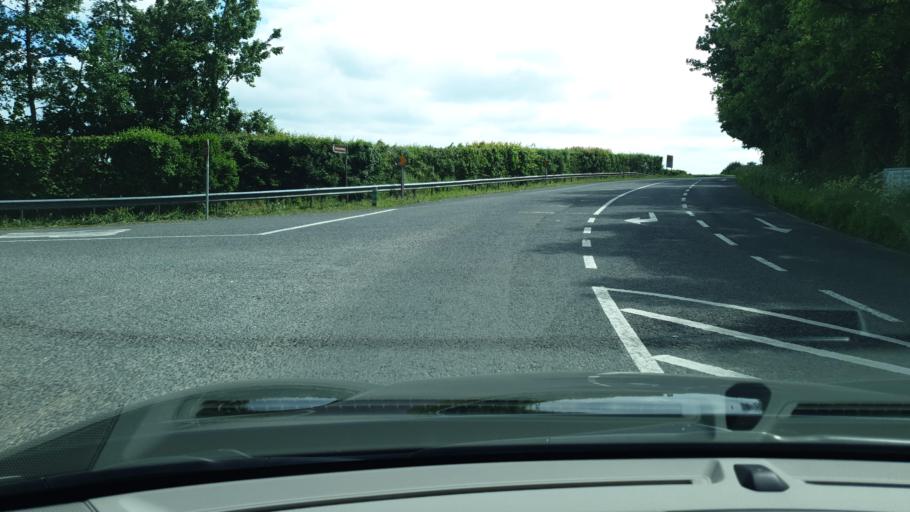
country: IE
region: Ulster
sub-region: An Cabhan
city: Kingscourt
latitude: 53.8287
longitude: -6.7569
